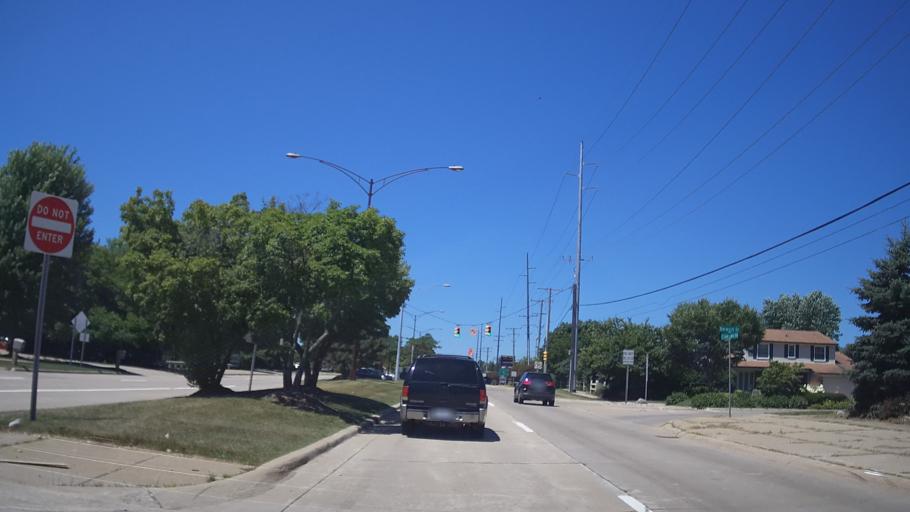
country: US
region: Michigan
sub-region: Oakland County
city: Troy
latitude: 42.5917
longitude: -83.1451
